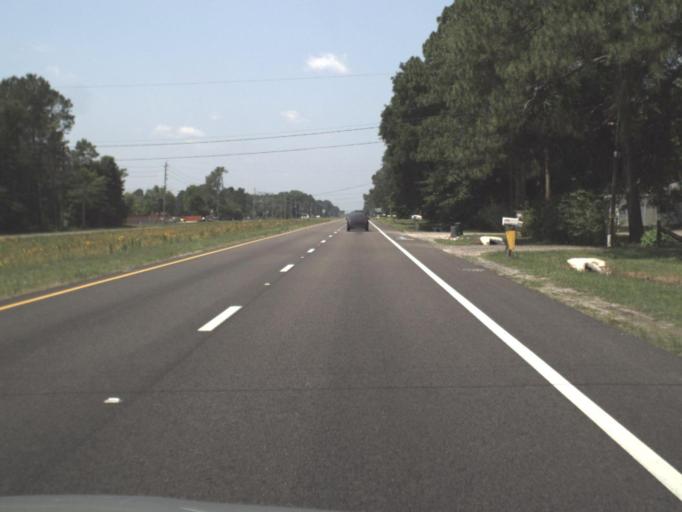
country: US
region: Florida
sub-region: Clay County
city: Bellair-Meadowbrook Terrace
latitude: 30.2711
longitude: -81.8409
